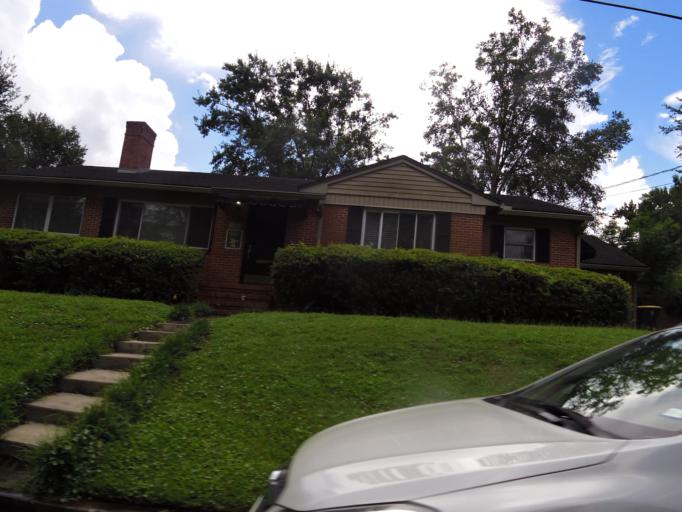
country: US
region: Florida
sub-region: Duval County
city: Jacksonville
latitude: 30.2958
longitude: -81.6447
